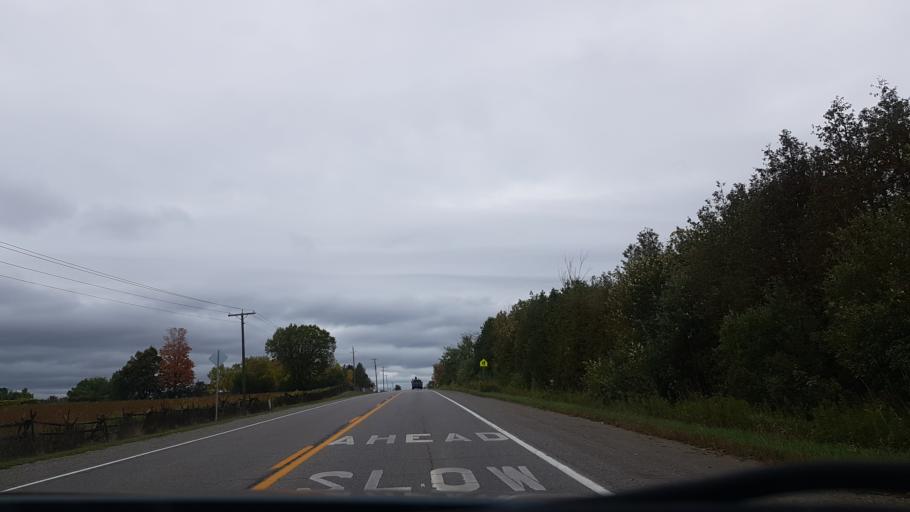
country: CA
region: Ontario
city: Omemee
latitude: 44.2338
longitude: -78.4835
